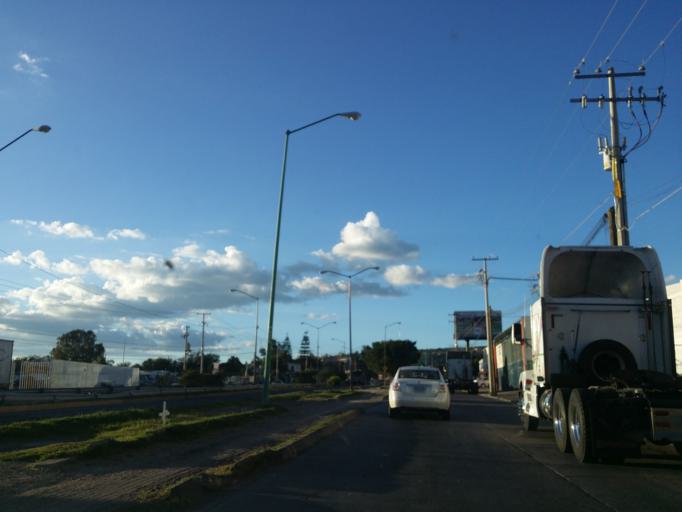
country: MX
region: Guanajuato
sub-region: Leon
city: Medina
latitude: 21.1941
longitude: -101.6664
